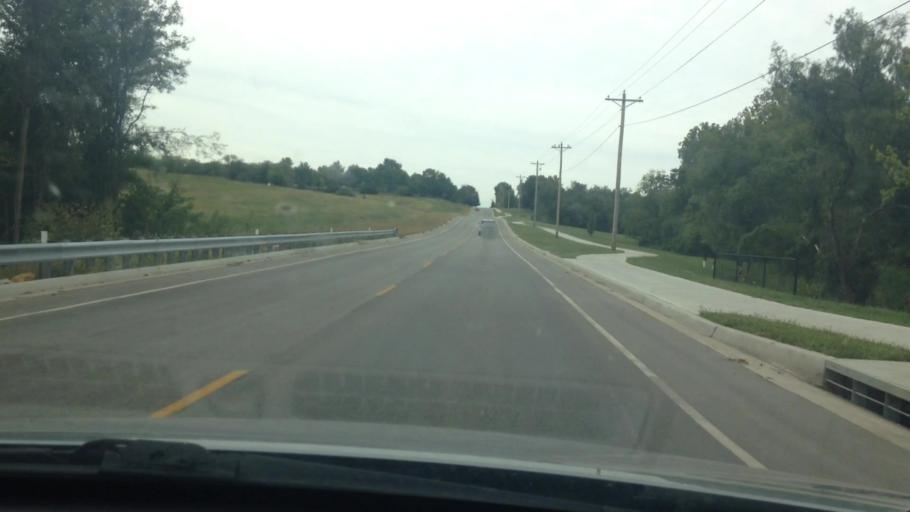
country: US
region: Missouri
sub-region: Platte County
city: Platte City
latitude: 39.3420
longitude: -94.7793
